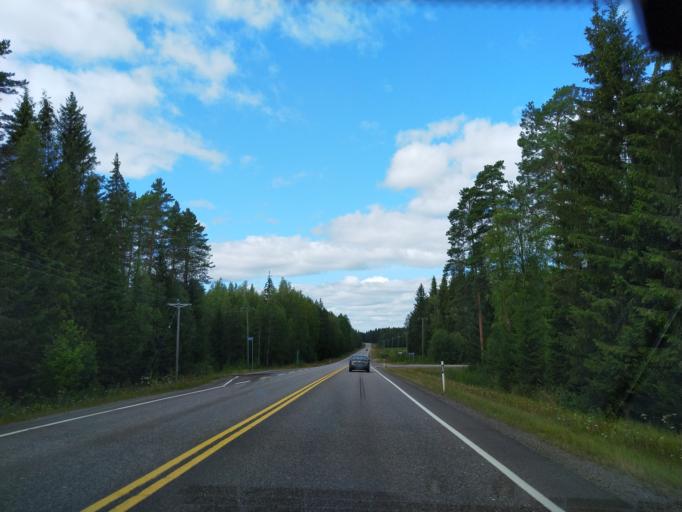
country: FI
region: Haeme
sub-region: Haemeenlinna
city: Renko
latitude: 60.7533
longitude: 24.3057
